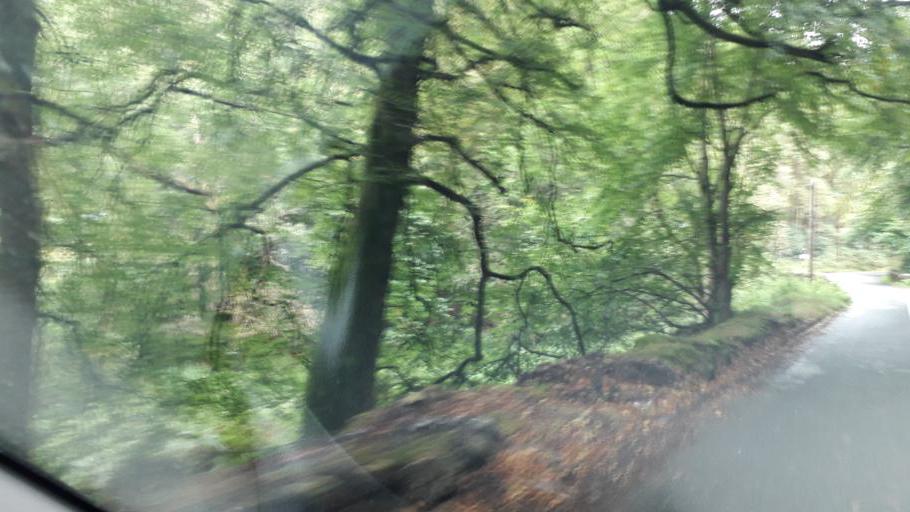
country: IE
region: Leinster
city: Ballyboden
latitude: 53.2429
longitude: -6.2959
